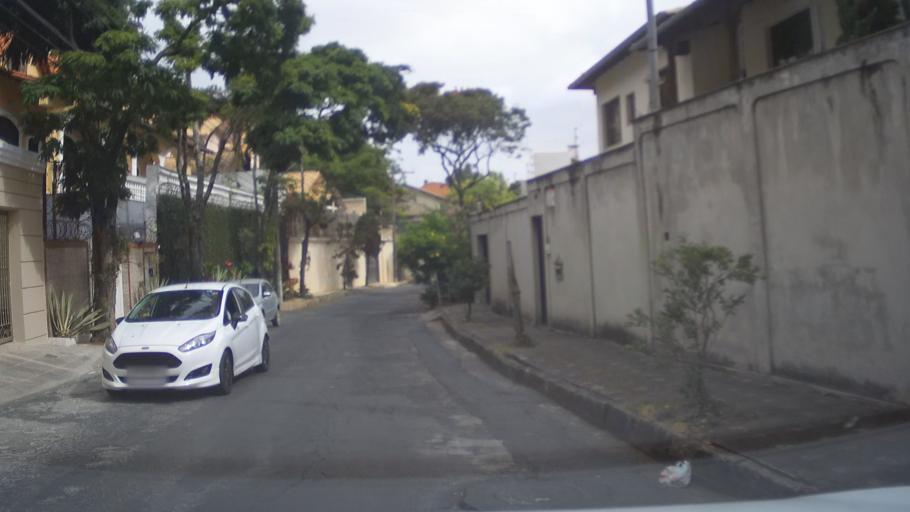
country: BR
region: Minas Gerais
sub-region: Belo Horizonte
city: Belo Horizonte
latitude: -19.9533
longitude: -43.9171
